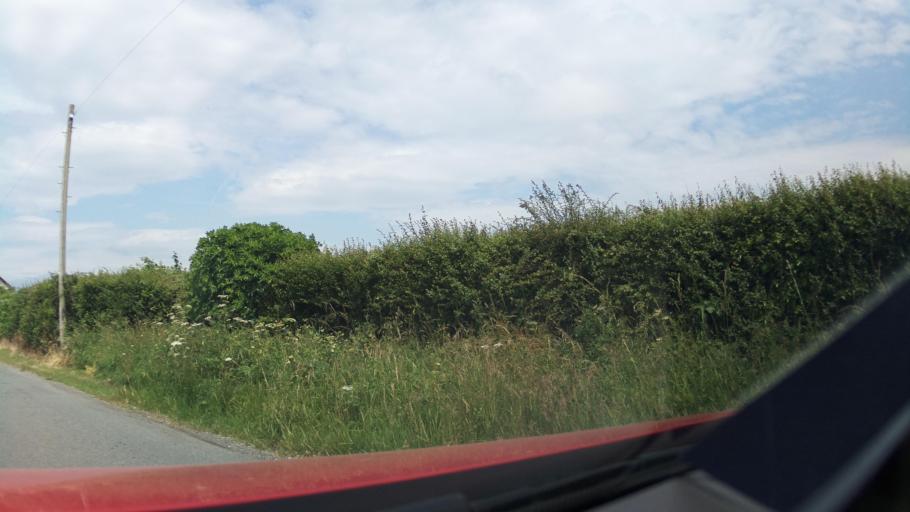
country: GB
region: Wales
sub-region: Vale of Glamorgan
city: Wick
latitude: 51.4385
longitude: -3.5679
